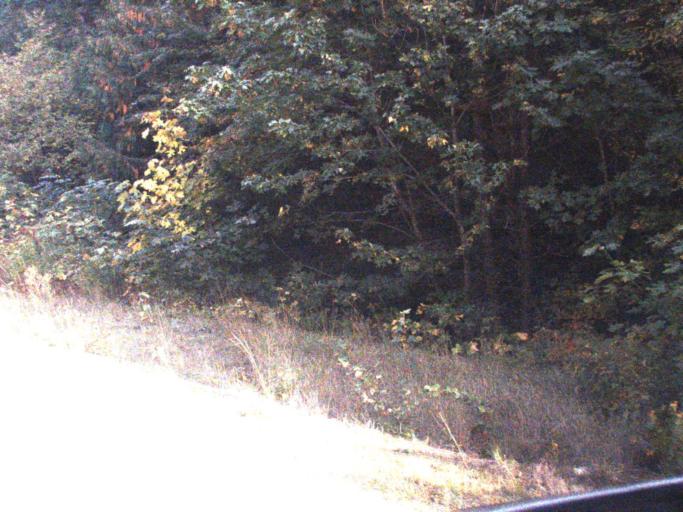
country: US
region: Washington
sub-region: Snohomish County
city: Darrington
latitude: 48.7053
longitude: -120.9299
